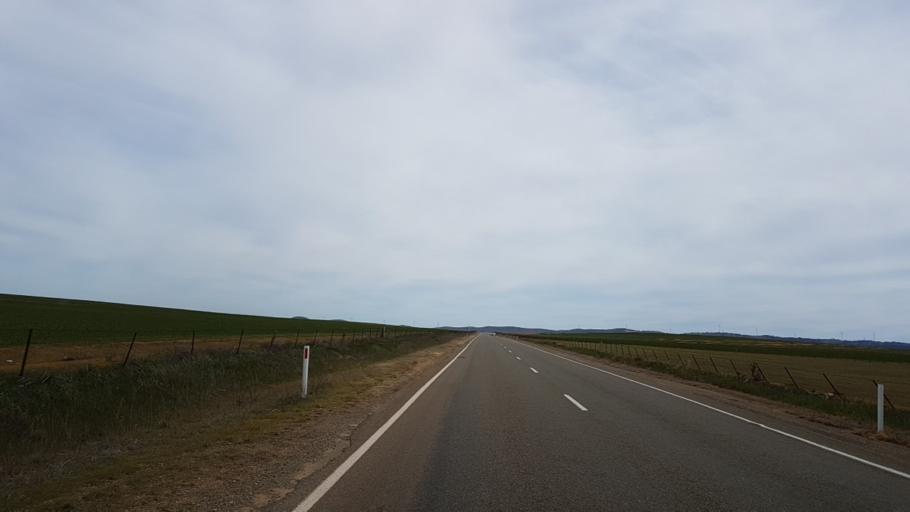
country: AU
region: South Australia
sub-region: Peterborough
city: Peterborough
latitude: -33.0220
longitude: 138.6813
